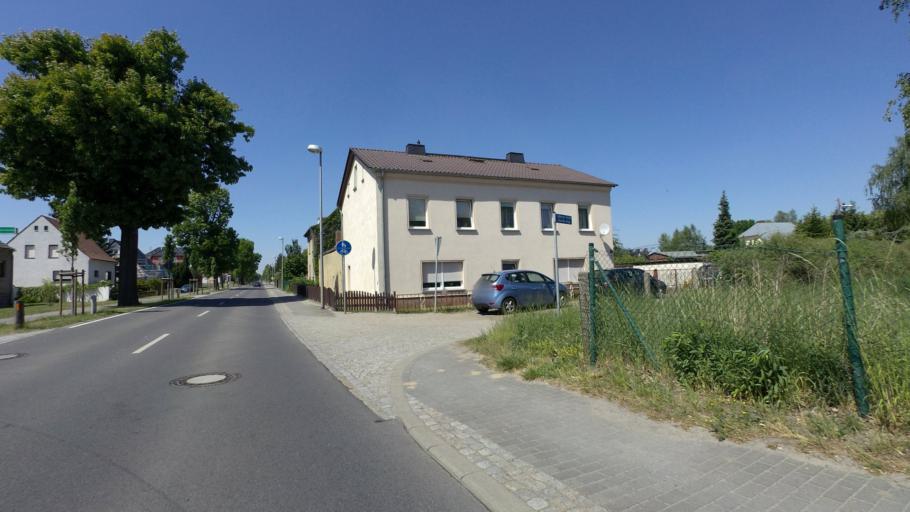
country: DE
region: Brandenburg
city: Peitz
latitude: 51.8605
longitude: 14.4026
